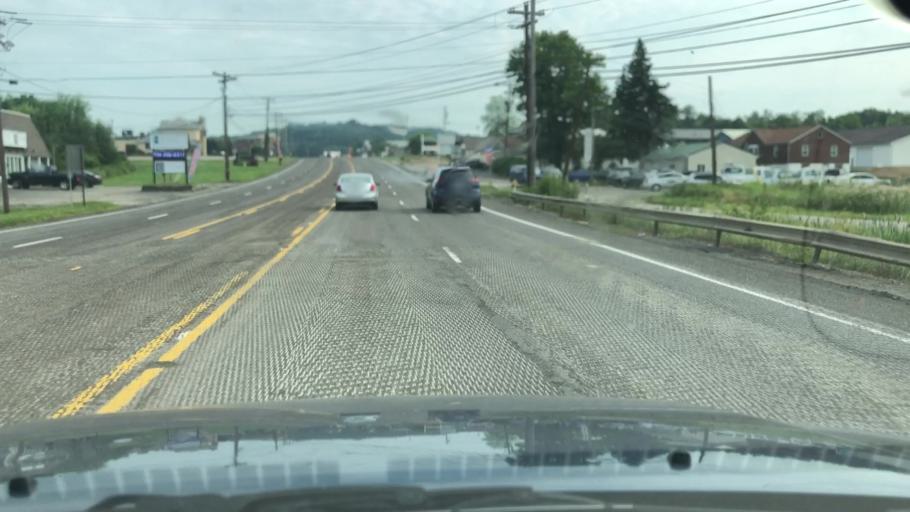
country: US
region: Pennsylvania
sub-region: Butler County
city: Nixon
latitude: 40.7575
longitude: -79.9240
